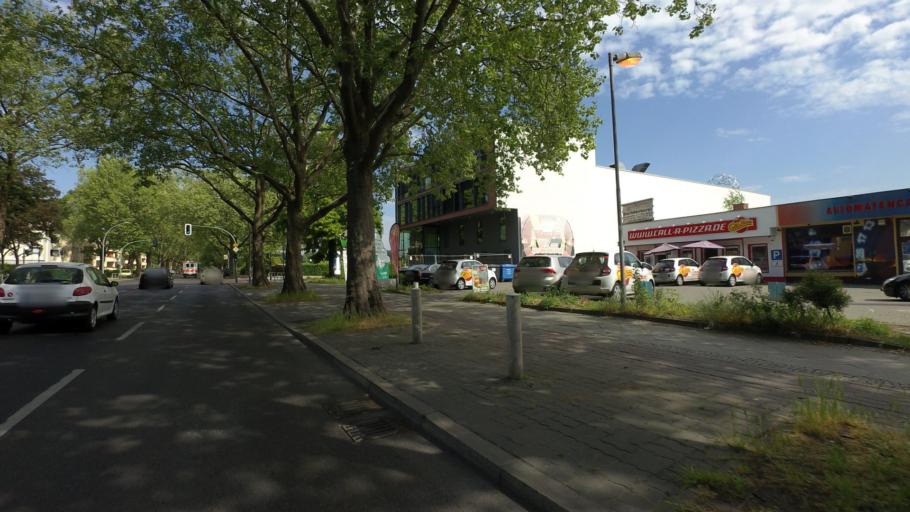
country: DE
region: Berlin
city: Reinickendorf
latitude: 52.5807
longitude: 13.3456
